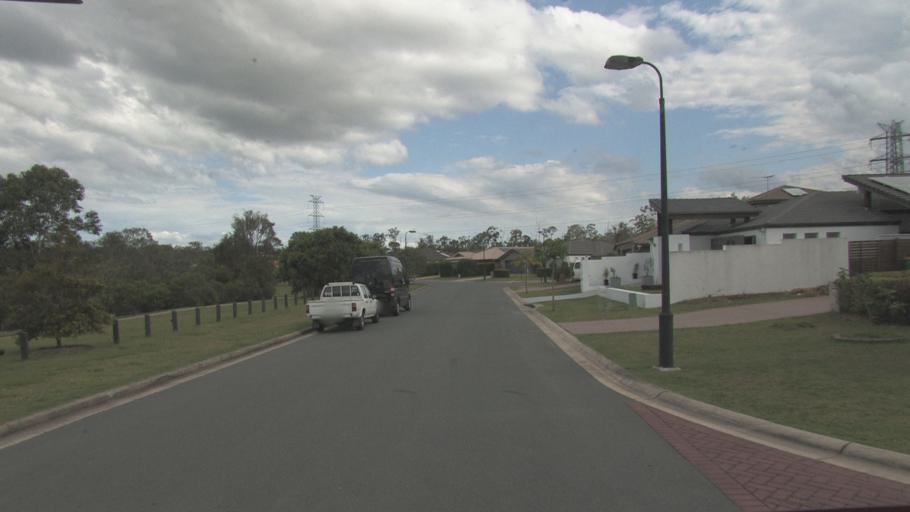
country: AU
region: Queensland
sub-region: Logan
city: Woodridge
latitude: -27.6589
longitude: 153.0764
